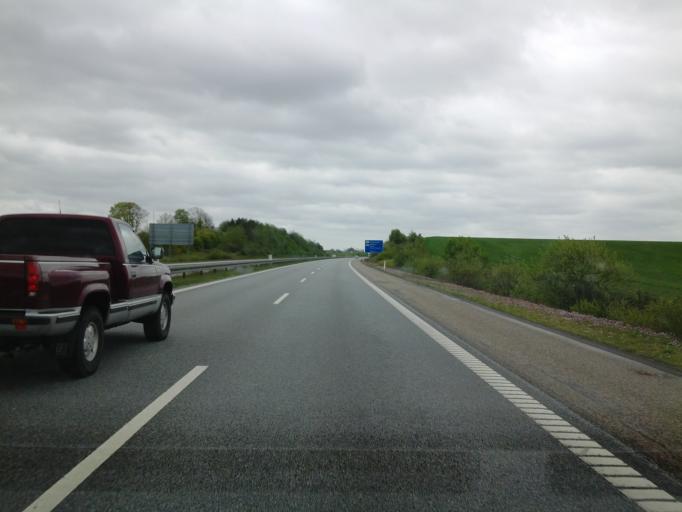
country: DK
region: North Denmark
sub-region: Bronderslev Kommune
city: Hjallerup
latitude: 57.1796
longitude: 10.1962
